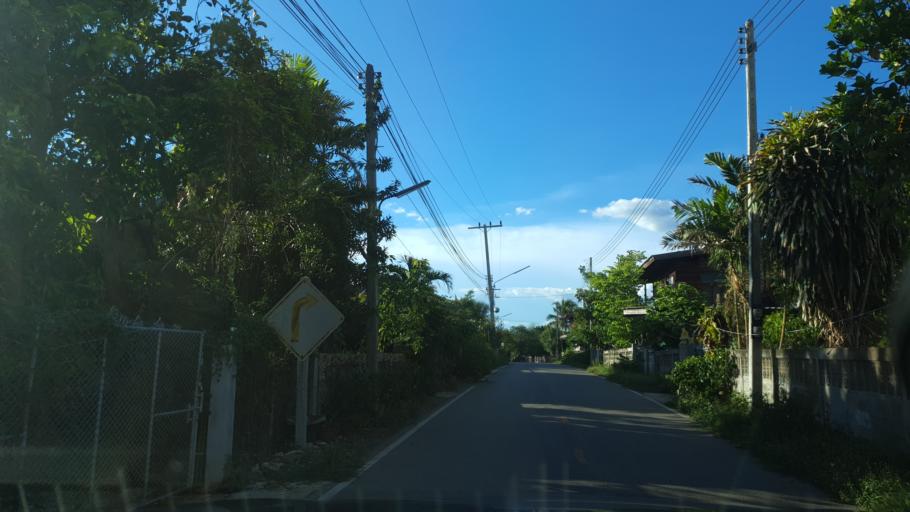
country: TH
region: Lampang
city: Sop Prap
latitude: 17.8897
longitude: 99.3112
